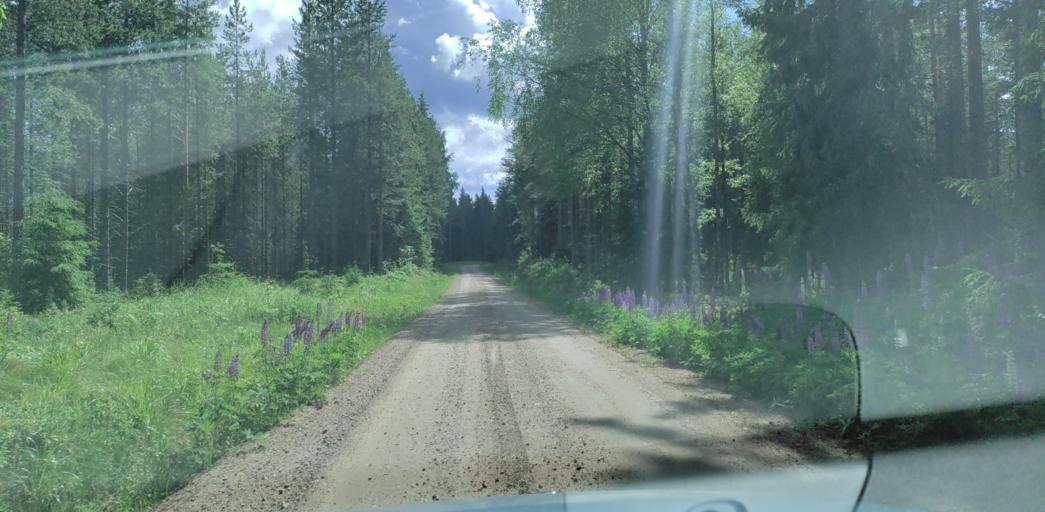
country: SE
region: Vaermland
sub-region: Hagfors Kommun
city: Ekshaerad
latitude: 60.0573
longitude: 13.3108
